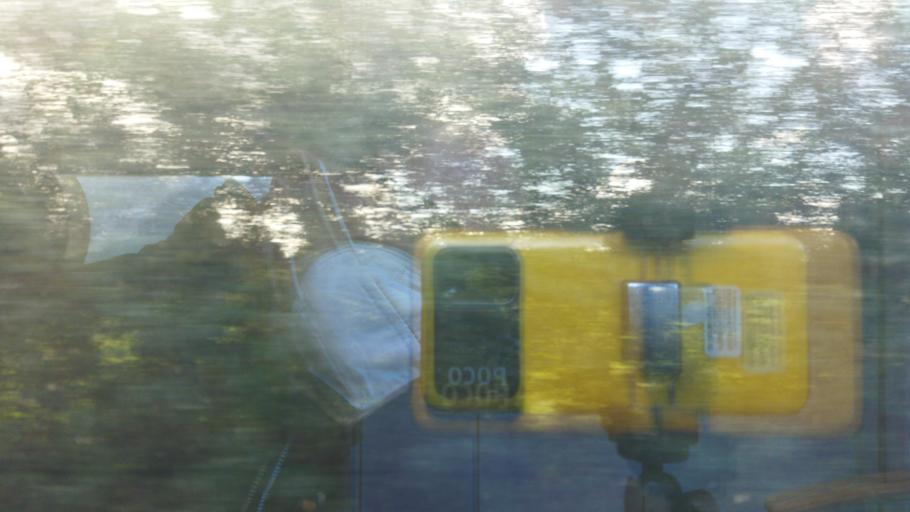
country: DE
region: Lower Saxony
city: Emden
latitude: 53.3384
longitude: 7.2880
